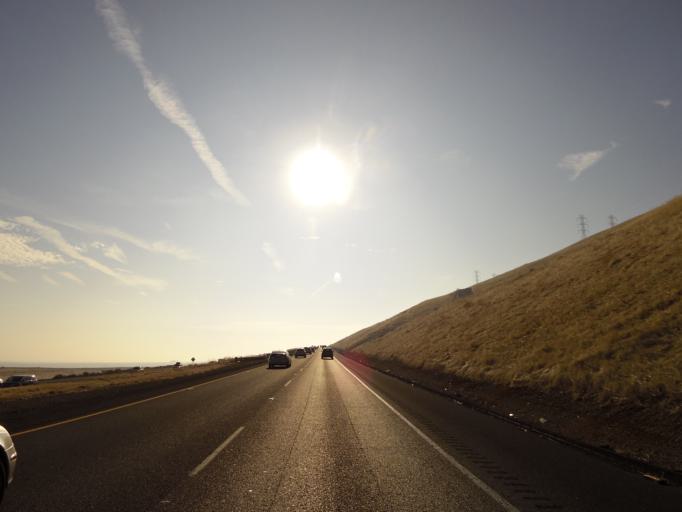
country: US
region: California
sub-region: Merced County
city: Los Banos
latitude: 36.9206
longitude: -120.8308
